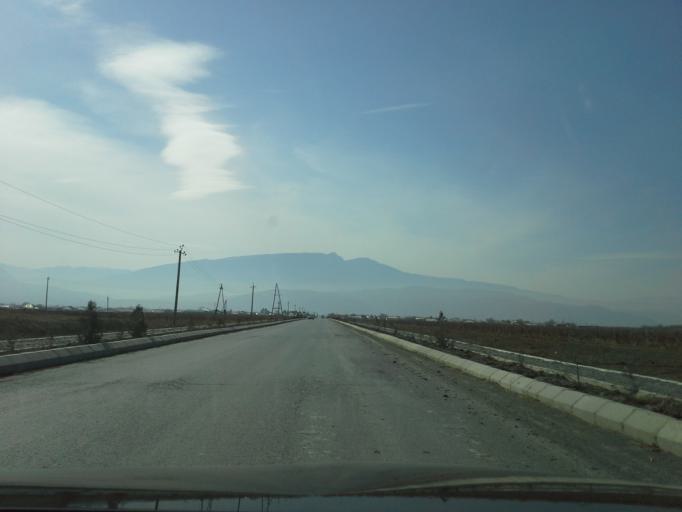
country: TM
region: Ahal
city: Abadan
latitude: 38.1196
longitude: 58.0404
